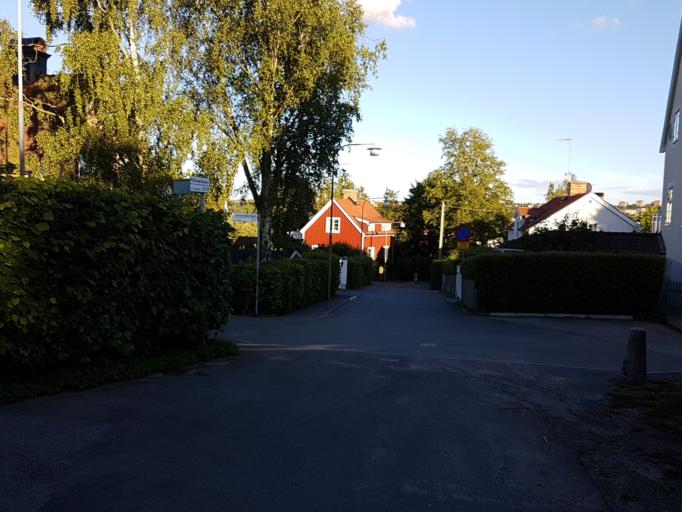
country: SE
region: Stockholm
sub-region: Stockholms Kommun
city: Bromma
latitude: 59.3212
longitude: 17.9686
